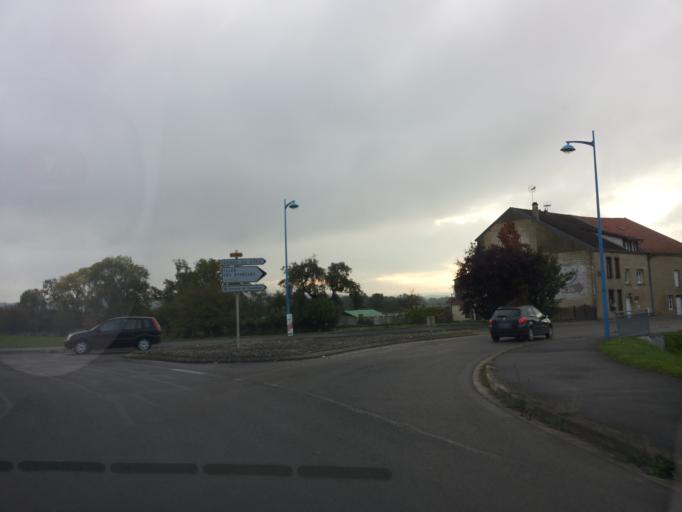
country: FR
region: Champagne-Ardenne
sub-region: Departement des Ardennes
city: Villers-Semeuse
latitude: 49.7270
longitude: 4.7548
